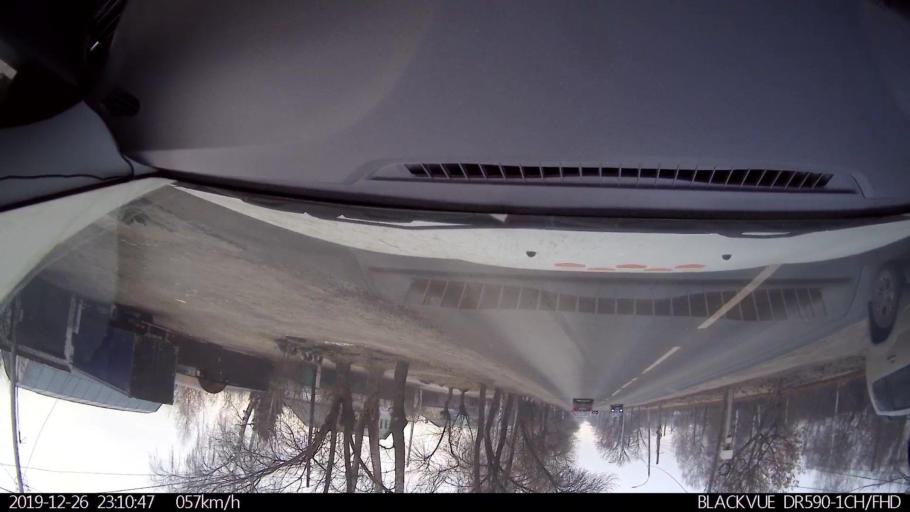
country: RU
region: Nizjnij Novgorod
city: Burevestnik
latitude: 56.2055
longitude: 43.7872
